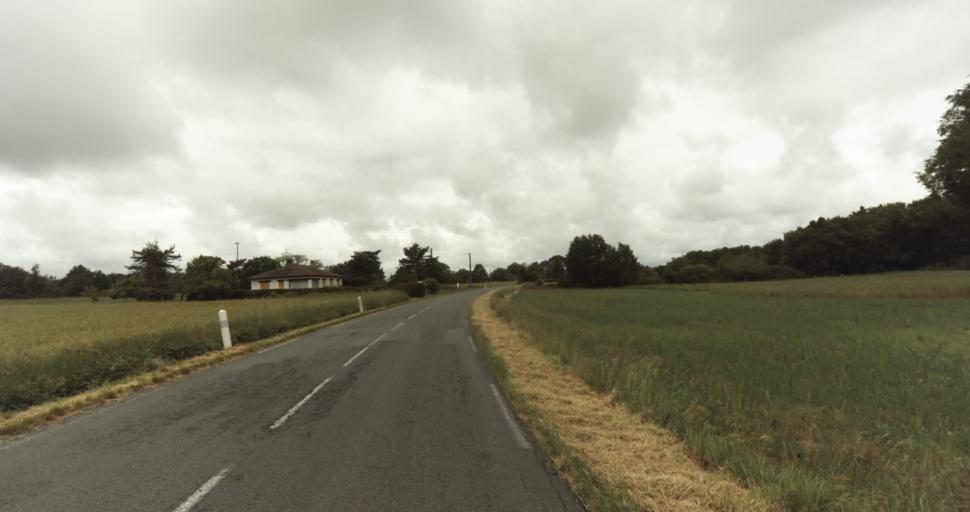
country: FR
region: Aquitaine
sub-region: Departement de la Dordogne
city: Beaumont-du-Perigord
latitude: 44.6967
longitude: 0.8542
